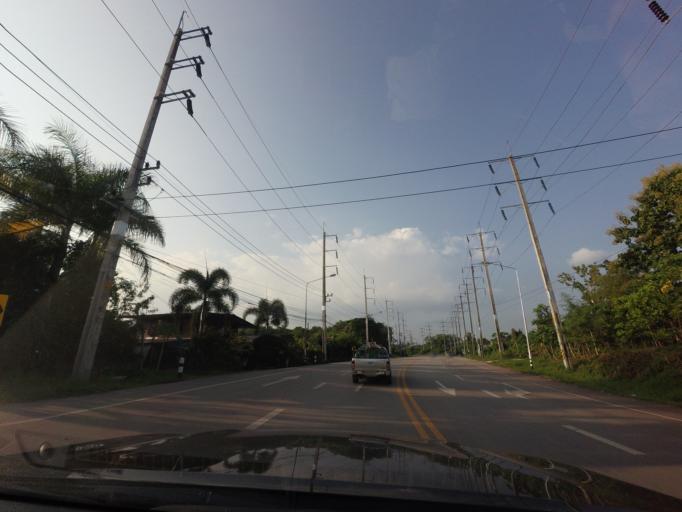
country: TH
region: Loei
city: Dan Sai
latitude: 17.2757
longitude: 101.1404
